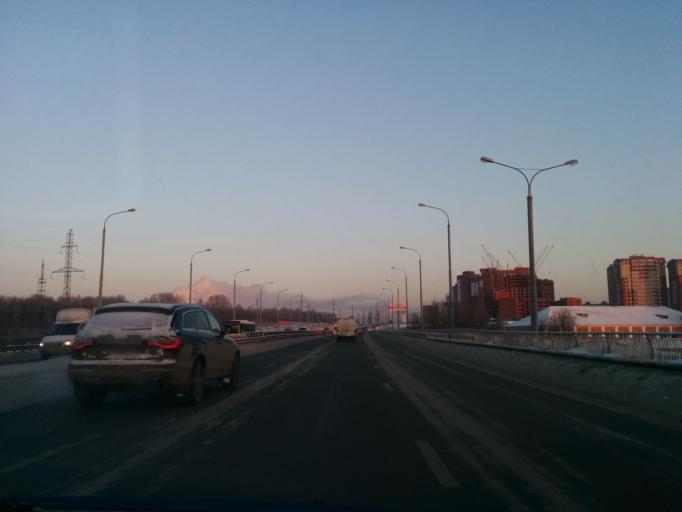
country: RU
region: Perm
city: Perm
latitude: 57.9861
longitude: 56.2731
